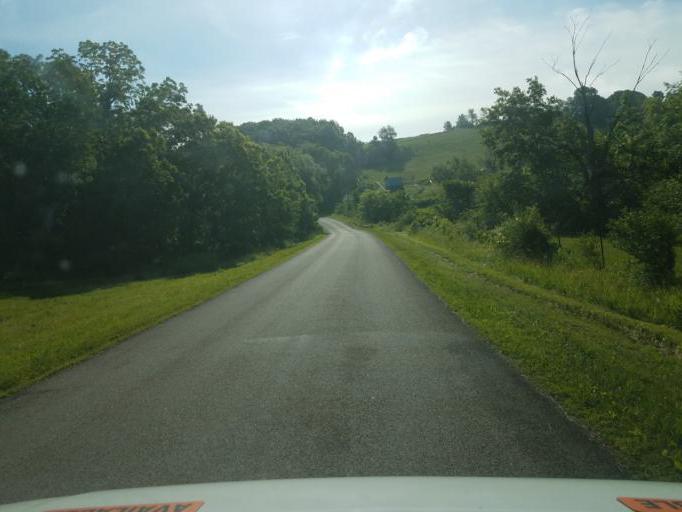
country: US
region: Wisconsin
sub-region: Sauk County
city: Reedsburg
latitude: 43.5801
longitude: -90.1491
